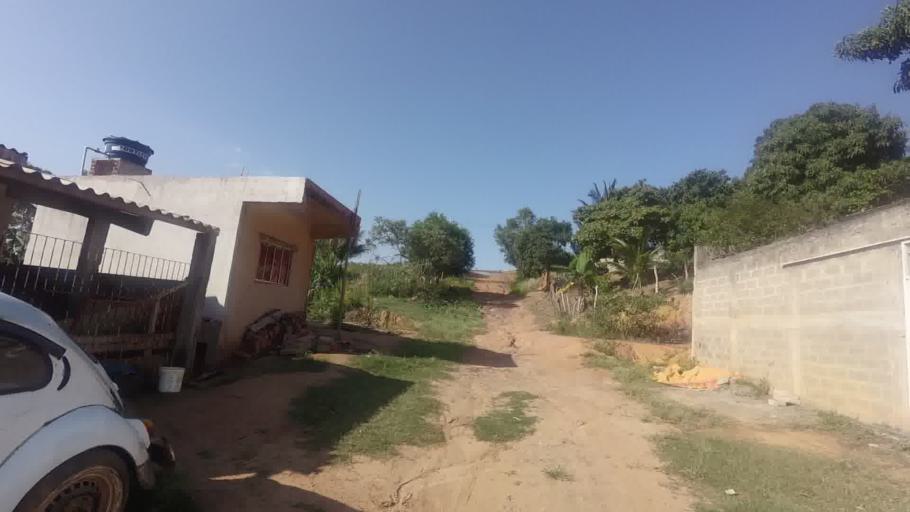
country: BR
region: Espirito Santo
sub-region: Guarapari
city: Guarapari
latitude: -20.7183
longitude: -40.5324
